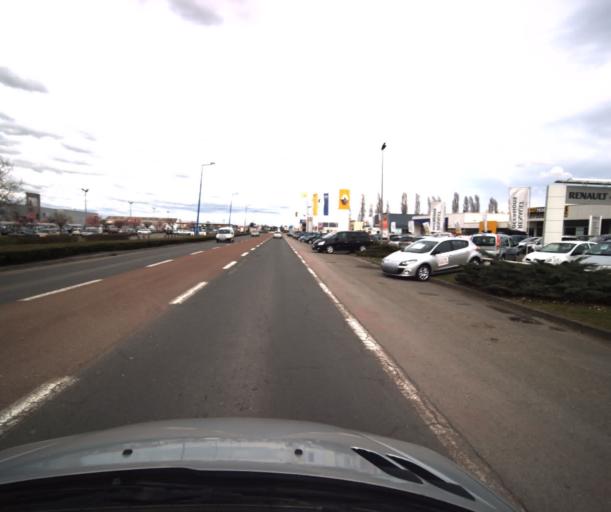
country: FR
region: Midi-Pyrenees
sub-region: Departement du Tarn-et-Garonne
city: Montauban
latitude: 44.0371
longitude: 1.3801
